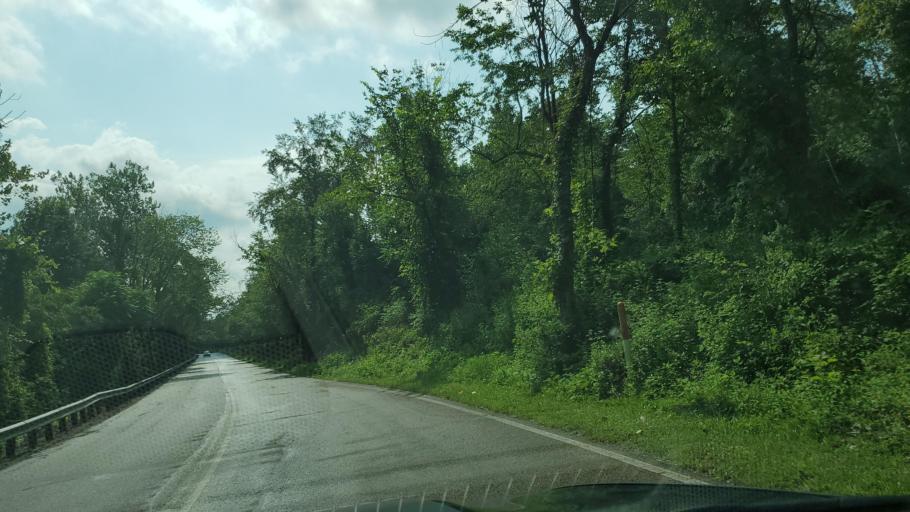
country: US
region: Ohio
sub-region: Mahoning County
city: Lowellville
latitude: 41.0390
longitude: -80.5451
